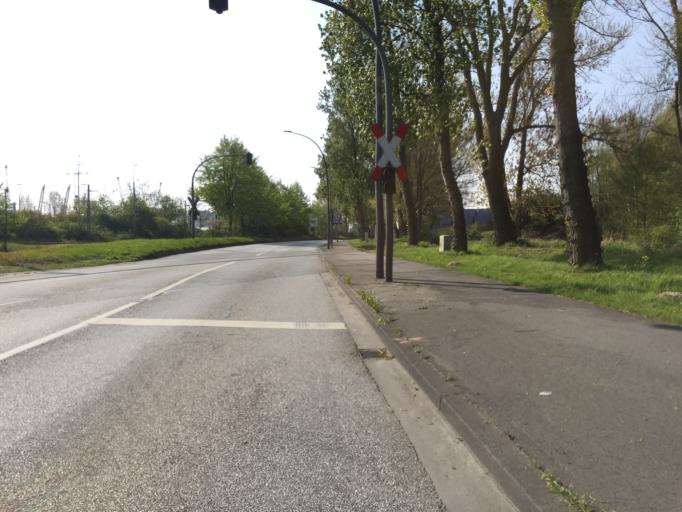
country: DE
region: Hamburg
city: Harburg
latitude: 53.4944
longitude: 9.9745
